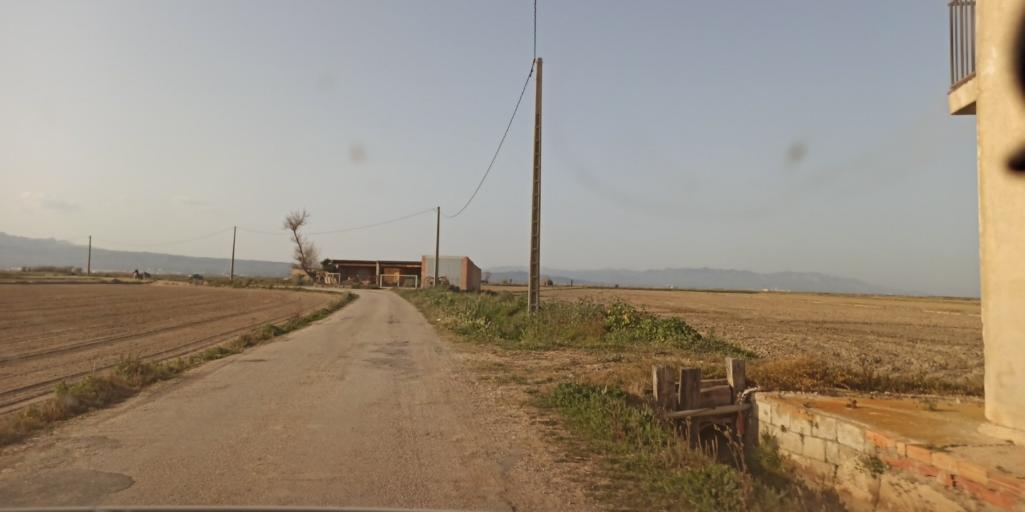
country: ES
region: Catalonia
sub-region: Provincia de Tarragona
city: Deltebre
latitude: 40.7544
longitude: 0.7549
